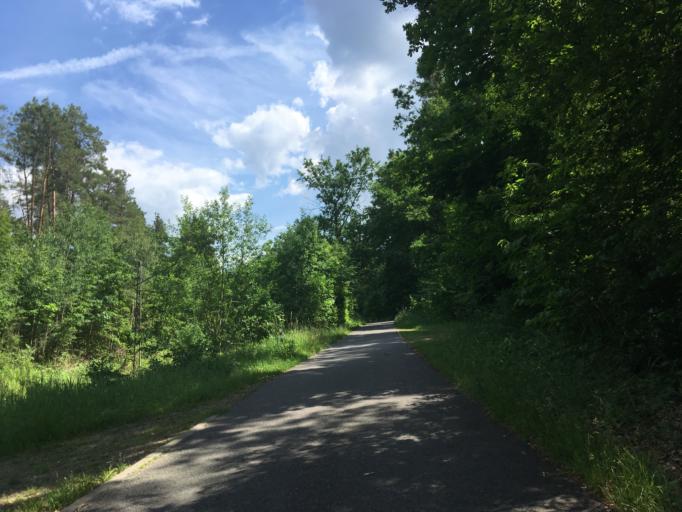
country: DE
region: Brandenburg
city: Waldsieversdorf
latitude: 52.5372
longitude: 14.0883
